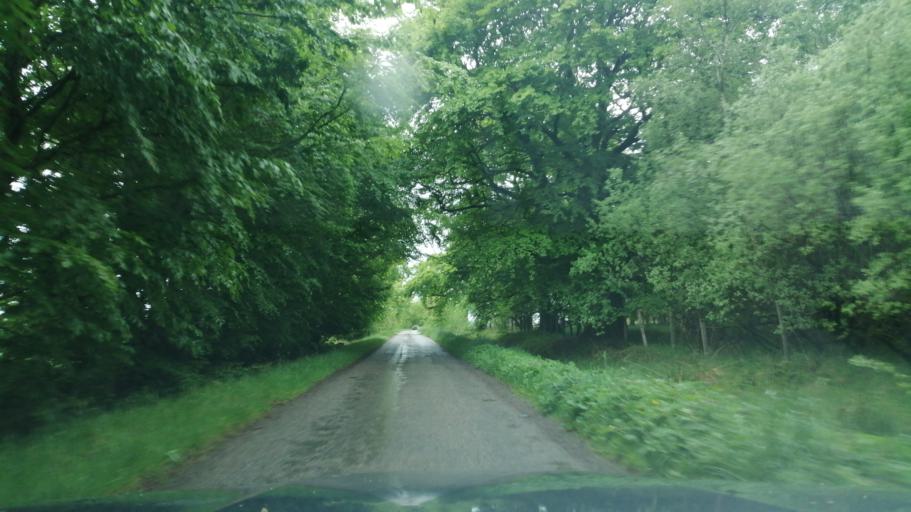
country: GB
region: Scotland
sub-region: Moray
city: Cullen
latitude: 57.5716
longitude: -2.8316
